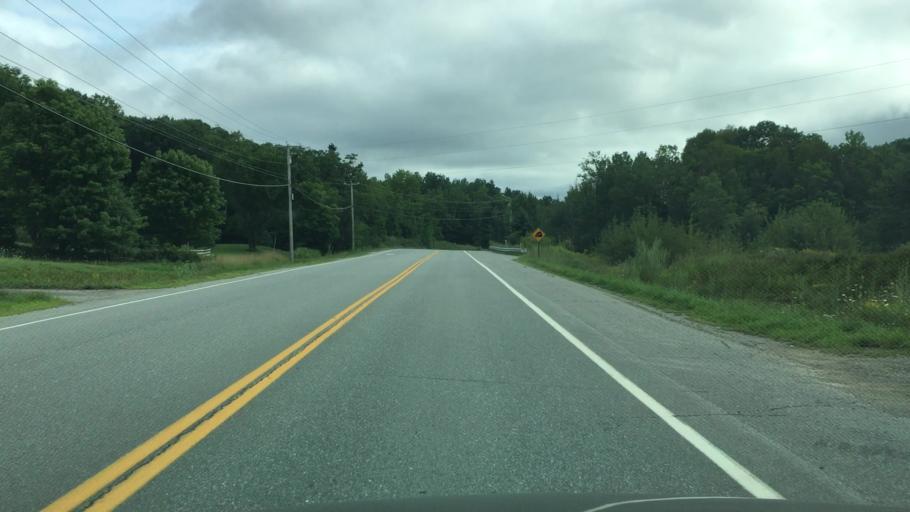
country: US
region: Maine
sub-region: Waldo County
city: Frankfort
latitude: 44.6152
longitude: -68.8696
